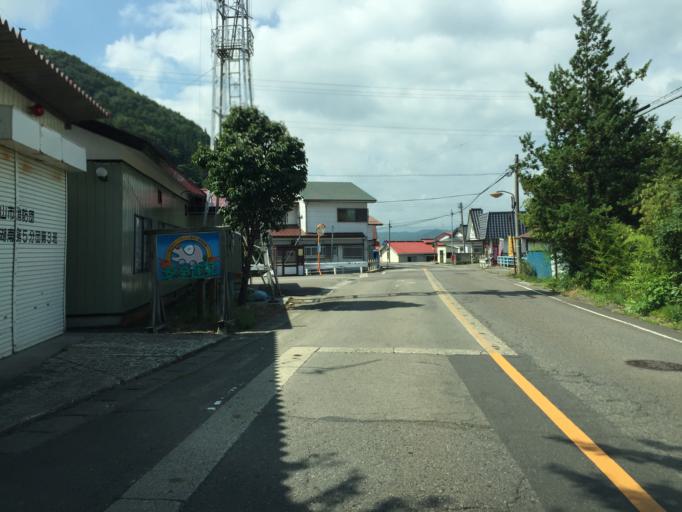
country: JP
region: Fukushima
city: Inawashiro
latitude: 37.4392
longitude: 140.1502
